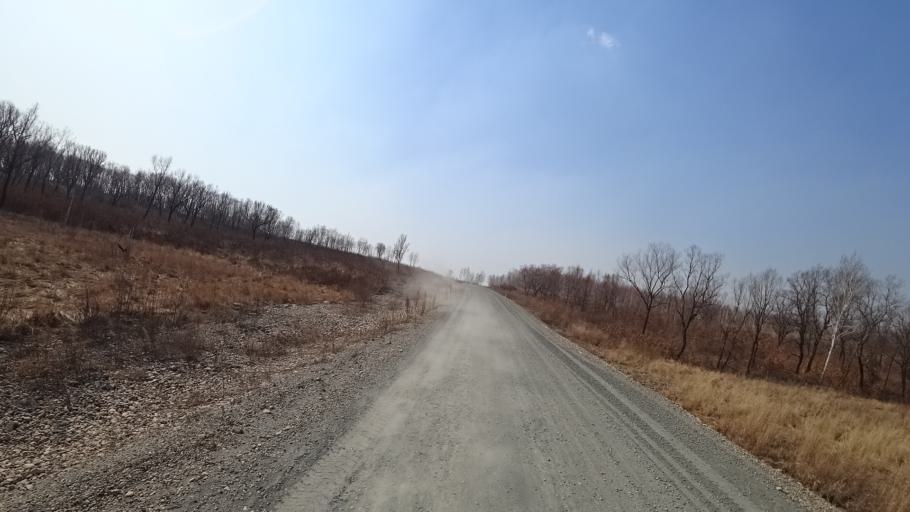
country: RU
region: Amur
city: Novobureyskiy
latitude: 49.8267
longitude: 129.9923
